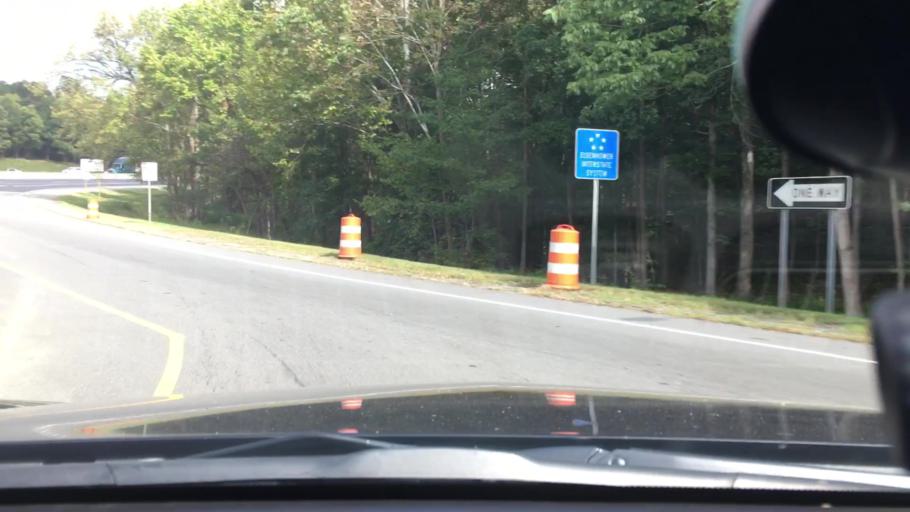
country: US
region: North Carolina
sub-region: Guilford County
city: Gibsonville
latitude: 36.0629
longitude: -79.5329
